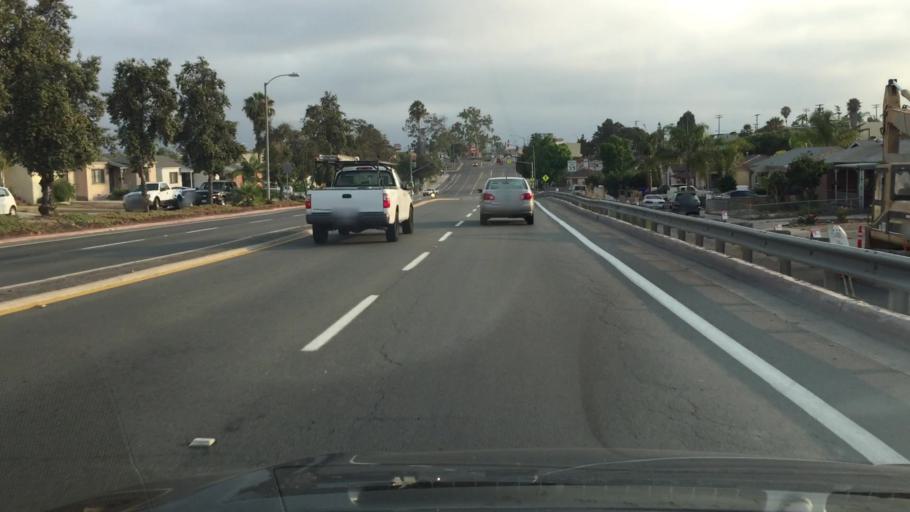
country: US
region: California
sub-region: San Diego County
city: National City
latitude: 32.7272
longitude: -117.0820
